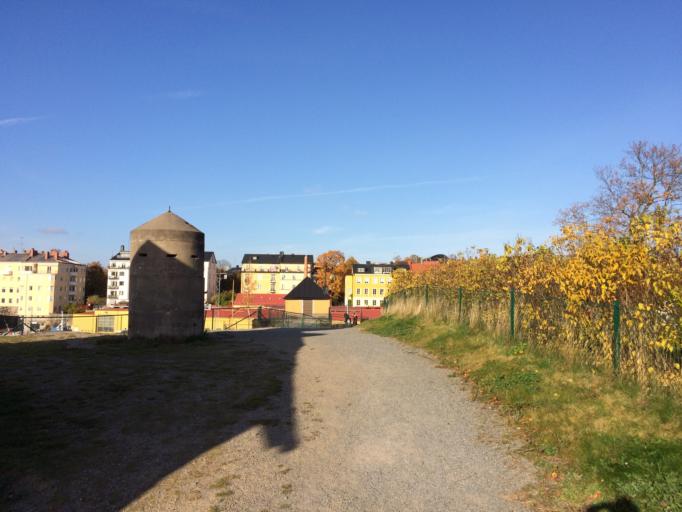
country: SE
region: Stockholm
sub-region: Stockholms Kommun
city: OEstermalm
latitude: 59.3210
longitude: 18.1006
